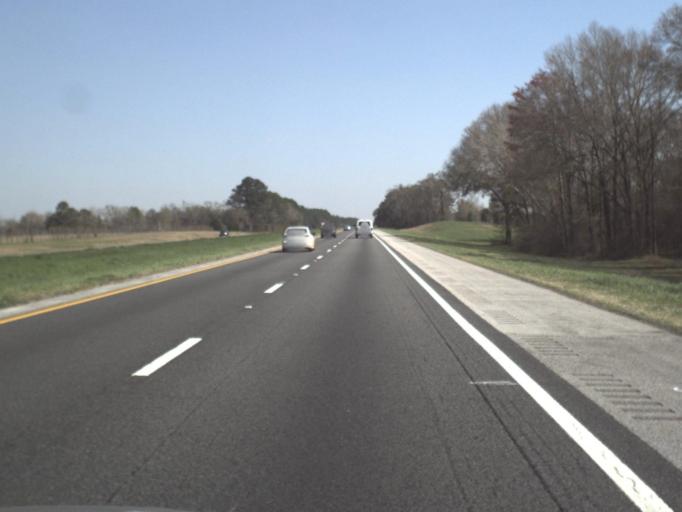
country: US
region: Florida
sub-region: Jackson County
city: Sneads
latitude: 30.6760
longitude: -85.0777
